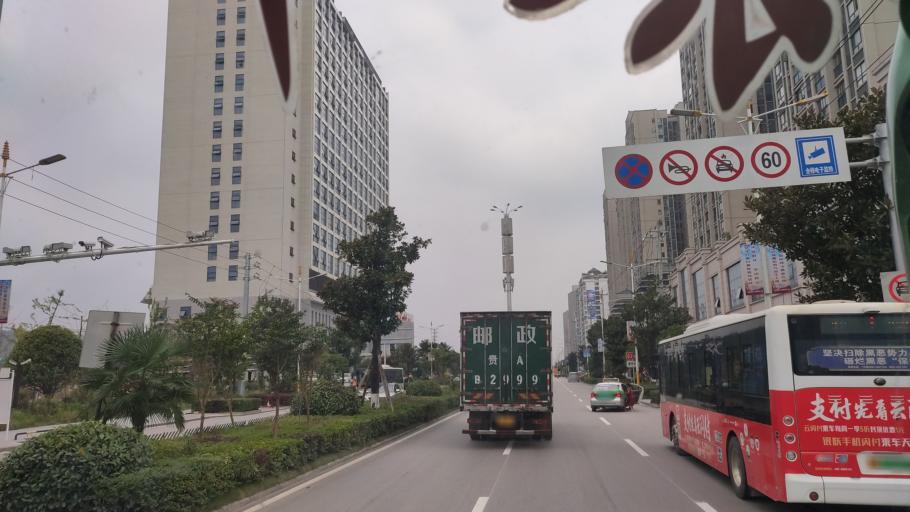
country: CN
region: Guizhou Sheng
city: Zhongchao
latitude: 26.2136
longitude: 109.1159
